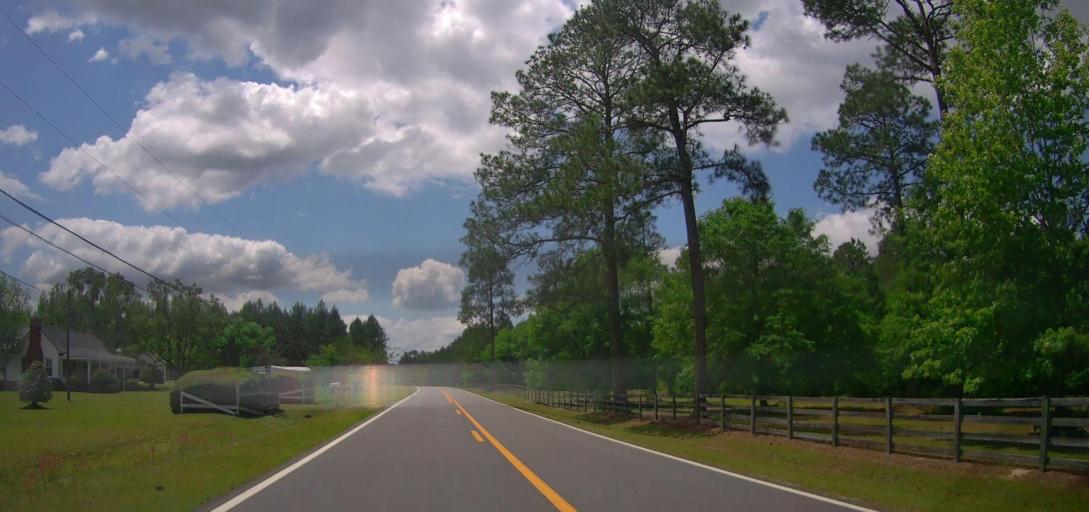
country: US
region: Georgia
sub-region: Laurens County
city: Dublin
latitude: 32.6034
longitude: -82.9025
